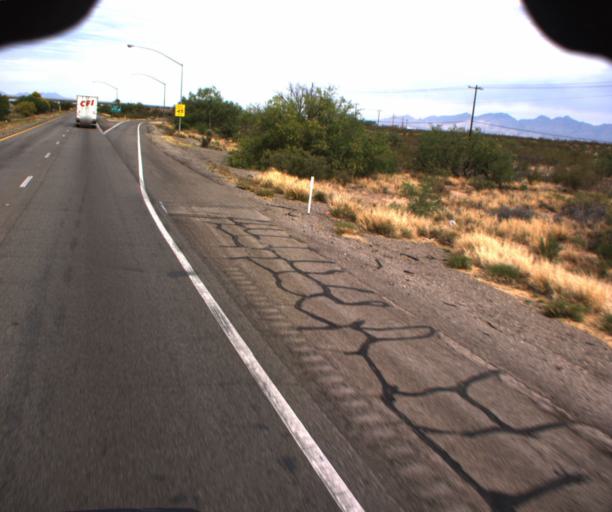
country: US
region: Arizona
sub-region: Pima County
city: Vail
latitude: 32.0594
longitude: -110.7700
